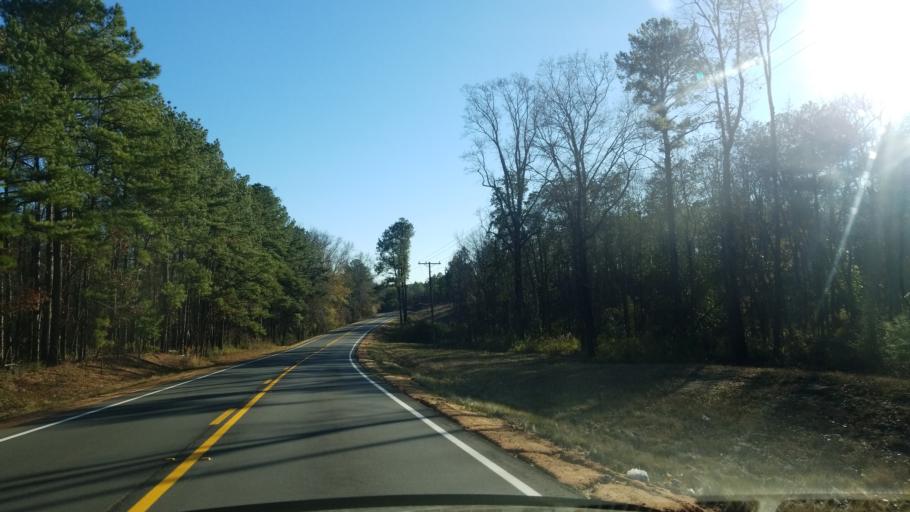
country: US
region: Georgia
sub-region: Talbot County
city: Talbotton
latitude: 32.5648
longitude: -84.5422
